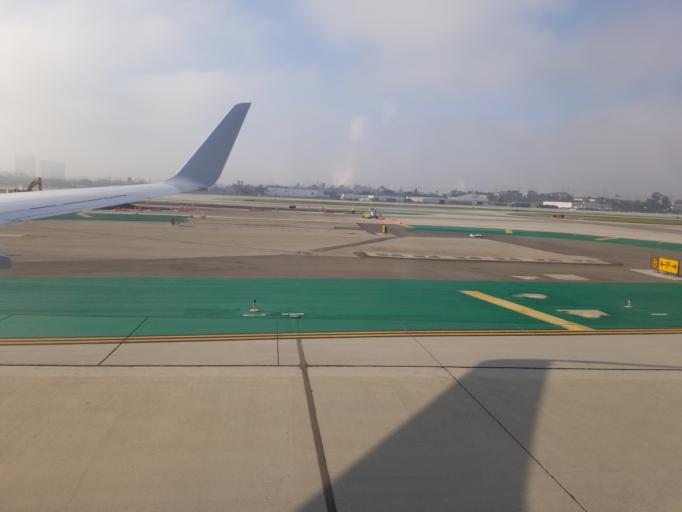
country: US
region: California
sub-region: Los Angeles County
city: El Segundo
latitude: 33.9379
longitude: -118.4083
